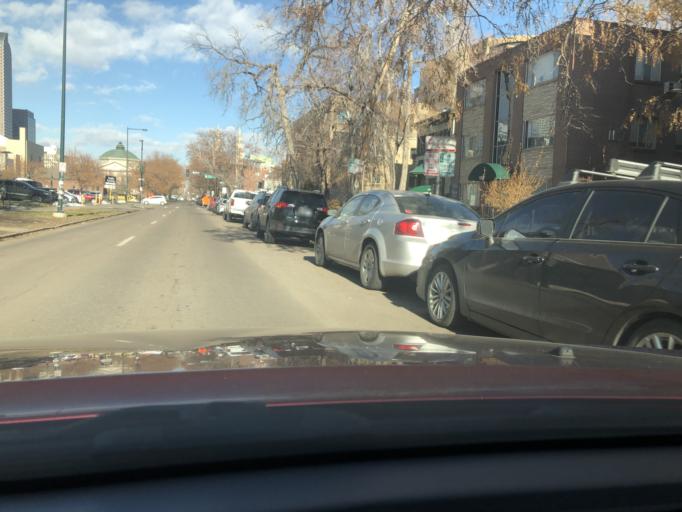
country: US
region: Colorado
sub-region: Denver County
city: Denver
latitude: 39.7360
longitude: -104.9823
